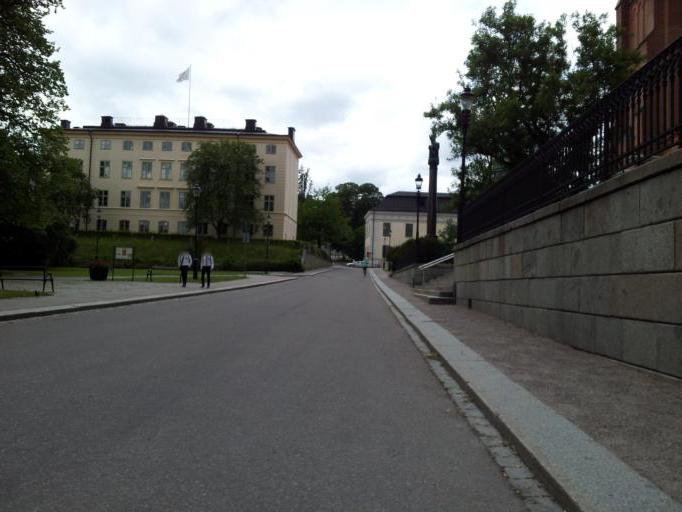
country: SE
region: Uppsala
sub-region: Uppsala Kommun
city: Uppsala
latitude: 59.8577
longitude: 17.6340
